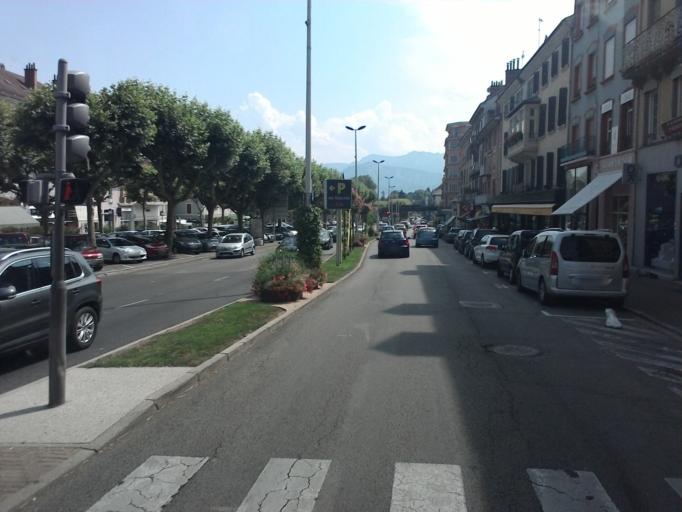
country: FR
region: Rhone-Alpes
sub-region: Departement de l'Isere
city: Voiron
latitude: 45.3671
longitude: 5.5911
